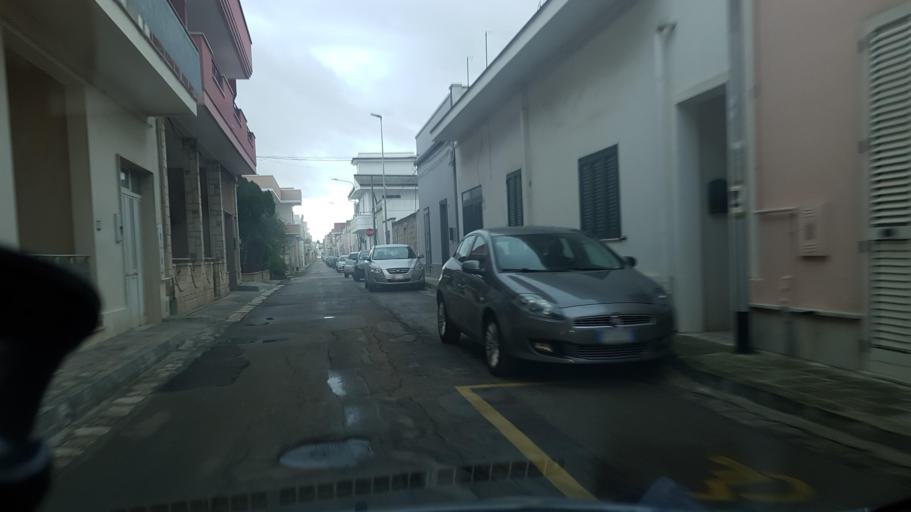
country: IT
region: Apulia
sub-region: Provincia di Lecce
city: Carmiano
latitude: 40.3464
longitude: 18.0383
